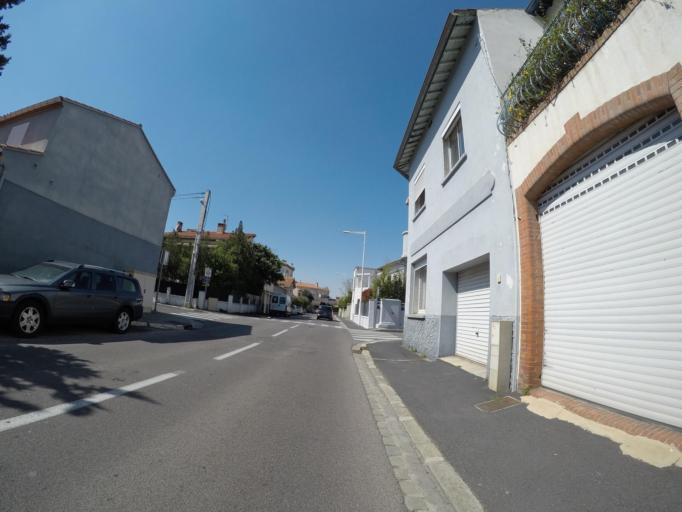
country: FR
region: Languedoc-Roussillon
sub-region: Departement des Pyrenees-Orientales
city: Perpignan
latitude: 42.6956
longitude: 2.9100
